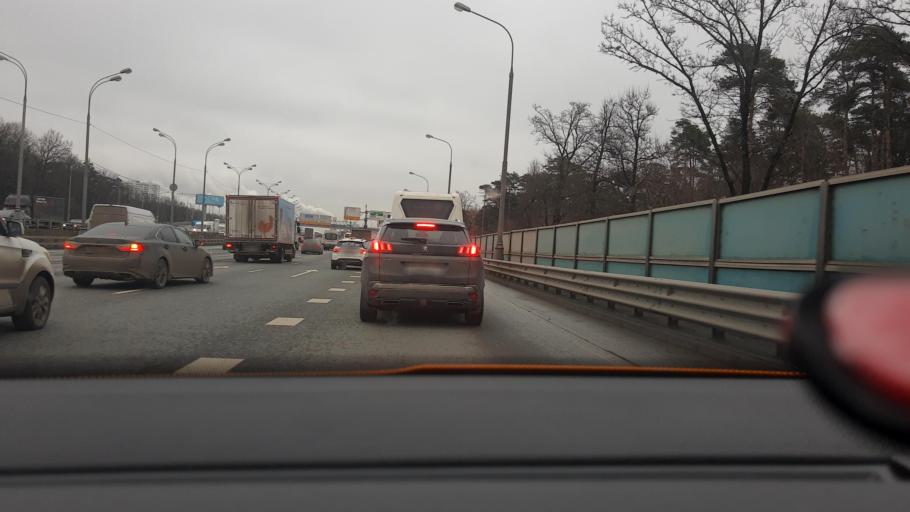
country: RU
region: Moskovskaya
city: Levoberezhnaya
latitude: 55.8828
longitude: 37.4667
